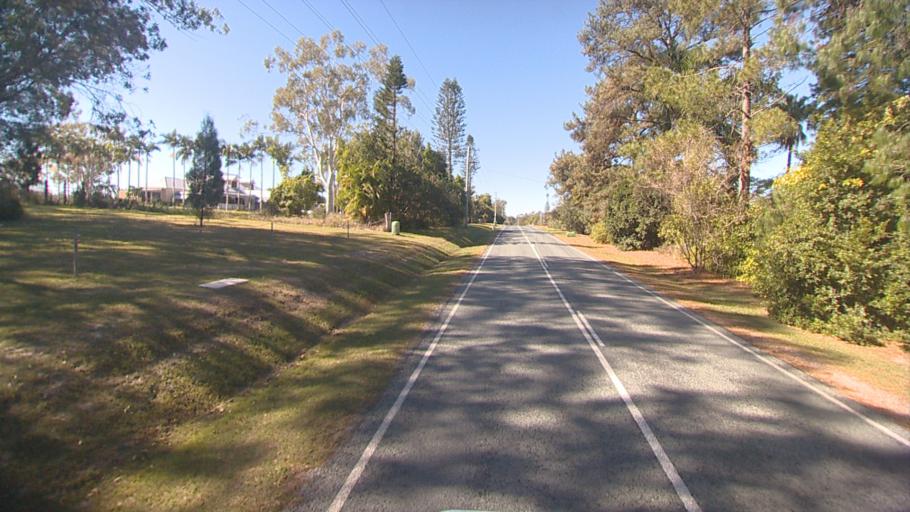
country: AU
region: Queensland
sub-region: Logan
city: Park Ridge South
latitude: -27.7183
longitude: 153.0537
